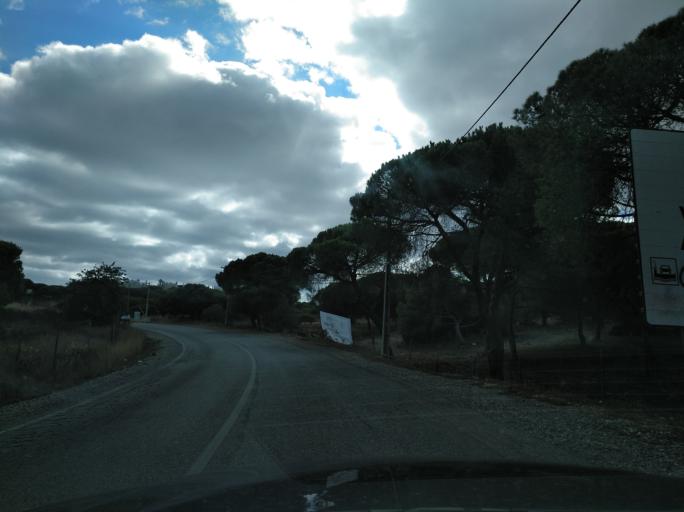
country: PT
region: Faro
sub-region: Vila Real de Santo Antonio
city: Monte Gordo
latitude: 37.1858
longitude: -7.4846
